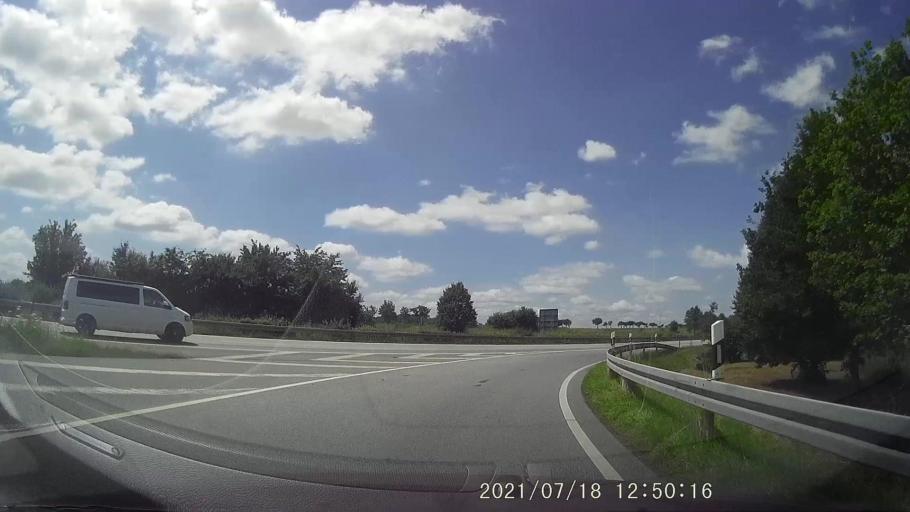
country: DE
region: Saxony
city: Reichenbach
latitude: 51.2051
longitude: 14.7602
